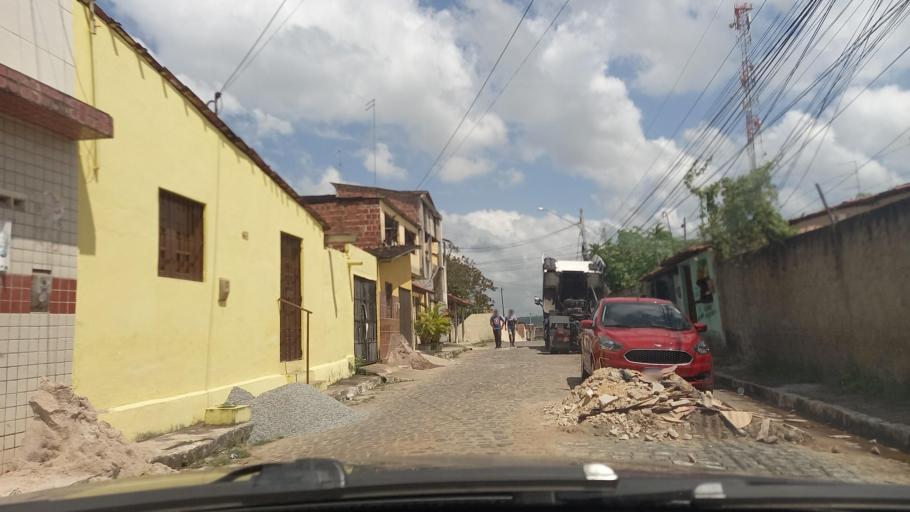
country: BR
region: Pernambuco
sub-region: Goiana
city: Goiana
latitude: -7.5632
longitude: -34.9987
